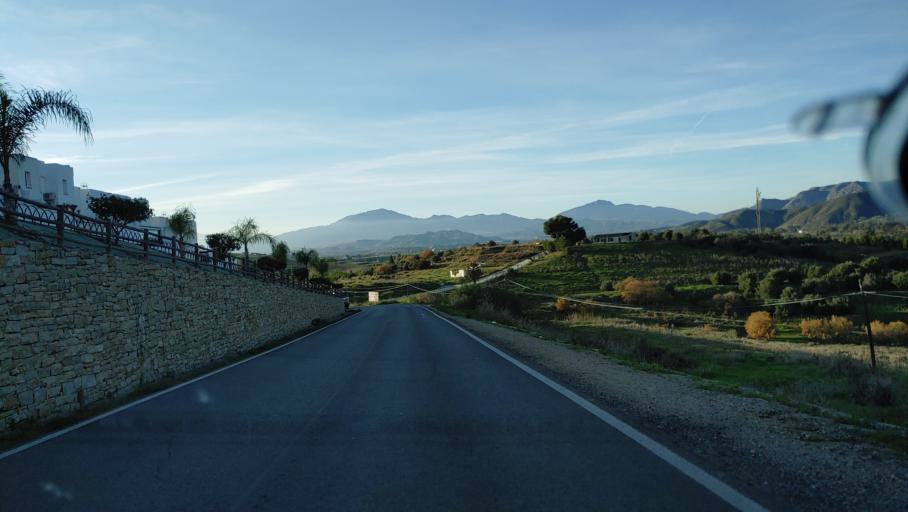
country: ES
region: Andalusia
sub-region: Provincia de Malaga
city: Cartama
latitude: 36.7121
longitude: -4.6374
